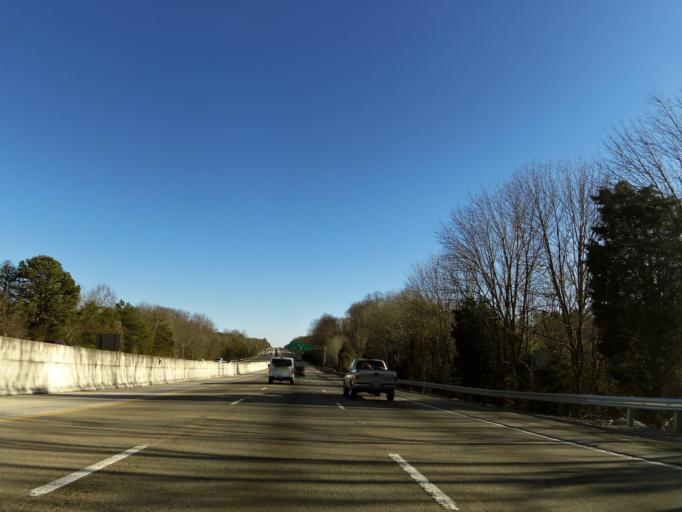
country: US
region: Tennessee
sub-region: Jefferson County
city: Dandridge
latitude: 36.0478
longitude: -83.4197
